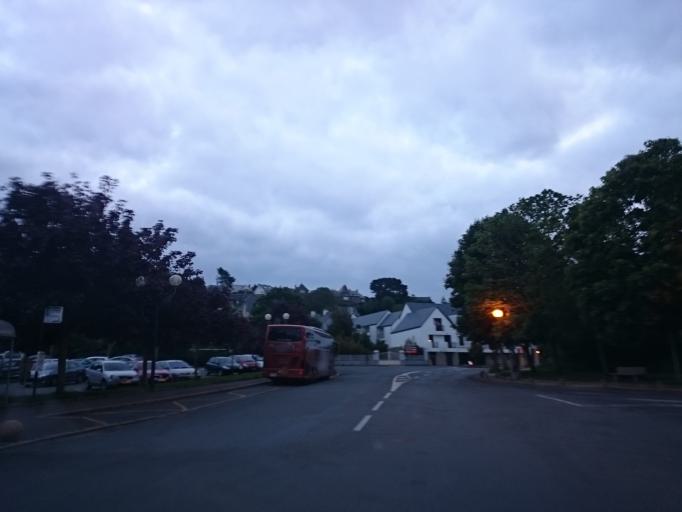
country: FR
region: Brittany
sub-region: Departement des Cotes-d'Armor
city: Perros-Guirec
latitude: 48.8149
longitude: -3.4589
